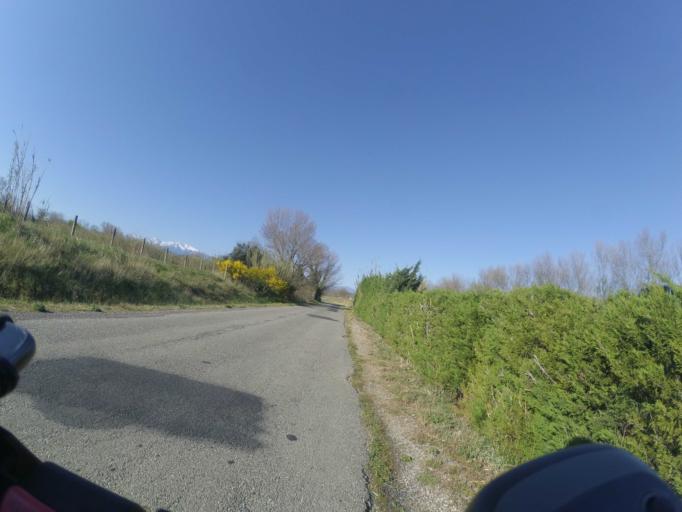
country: FR
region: Languedoc-Roussillon
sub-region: Departement des Pyrenees-Orientales
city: Millas
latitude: 42.6986
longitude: 2.6731
